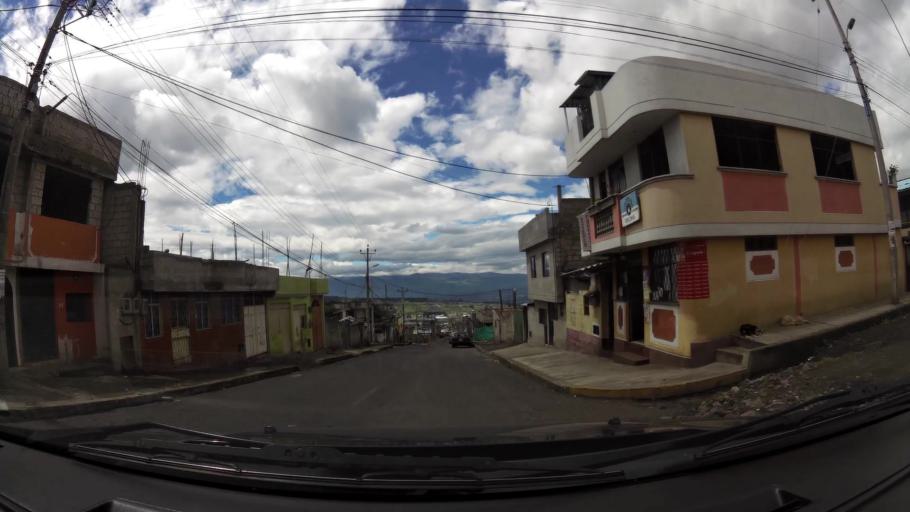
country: EC
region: Pichincha
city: Sangolqui
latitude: -0.3420
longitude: -78.5682
